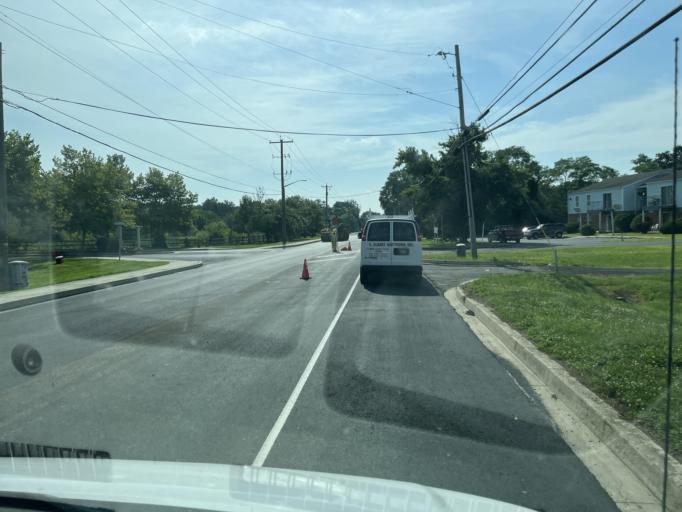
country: US
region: Maryland
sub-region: Dorchester County
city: Algonquin
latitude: 38.5678
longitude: -76.0965
